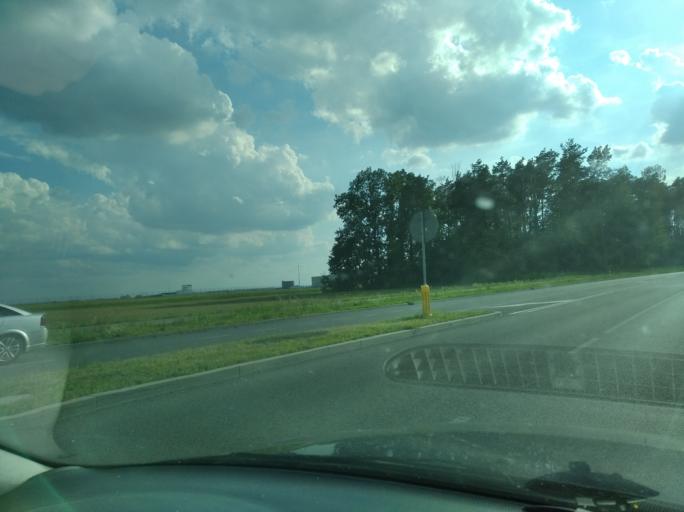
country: PL
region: Subcarpathian Voivodeship
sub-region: Powiat rzeszowski
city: Trzebownisko
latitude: 50.1160
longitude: 22.0172
